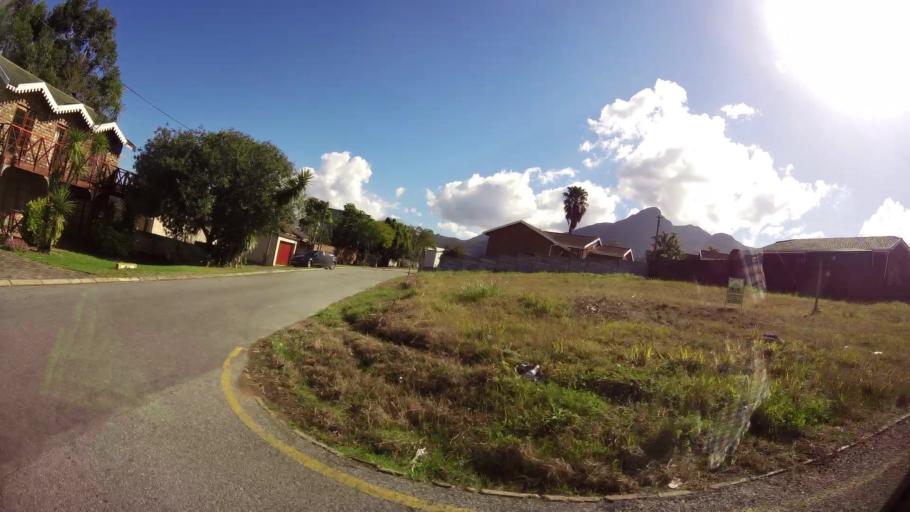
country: ZA
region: Western Cape
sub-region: Eden District Municipality
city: George
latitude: -33.9498
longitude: 22.4796
